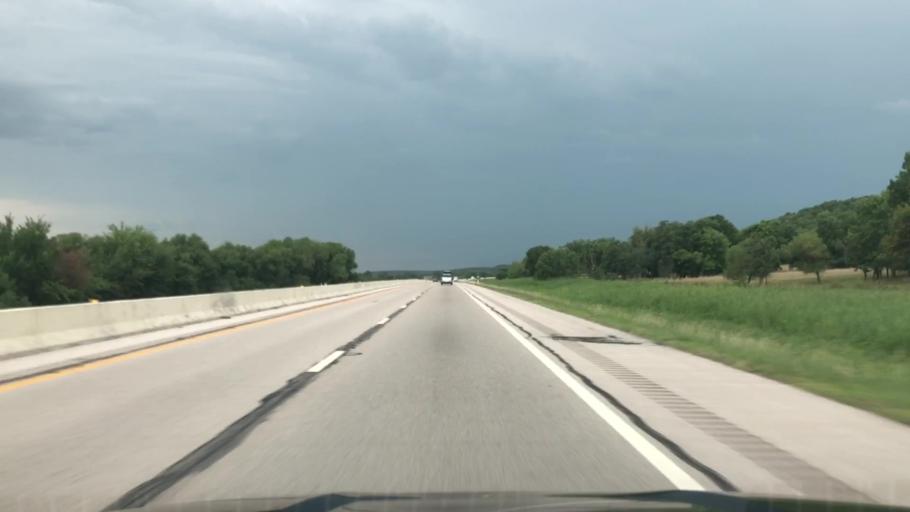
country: US
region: Oklahoma
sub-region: Rogers County
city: Bushyhead
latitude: 36.3605
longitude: -95.4533
